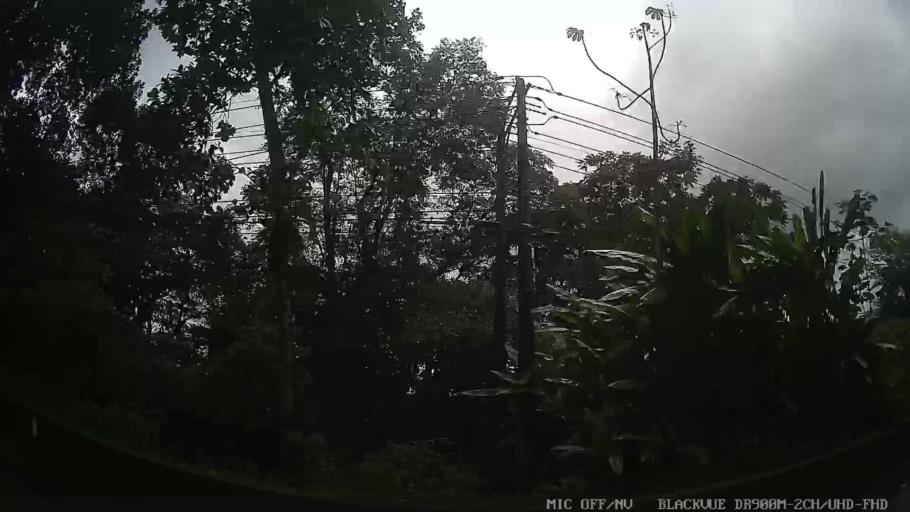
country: BR
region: Sao Paulo
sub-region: Santos
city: Santos
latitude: -23.8770
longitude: -46.3277
